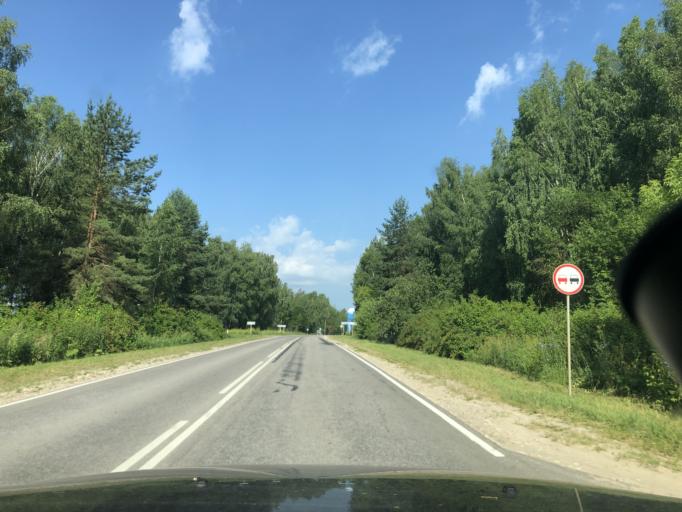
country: RU
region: Tula
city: Dubna
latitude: 54.1462
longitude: 36.9813
